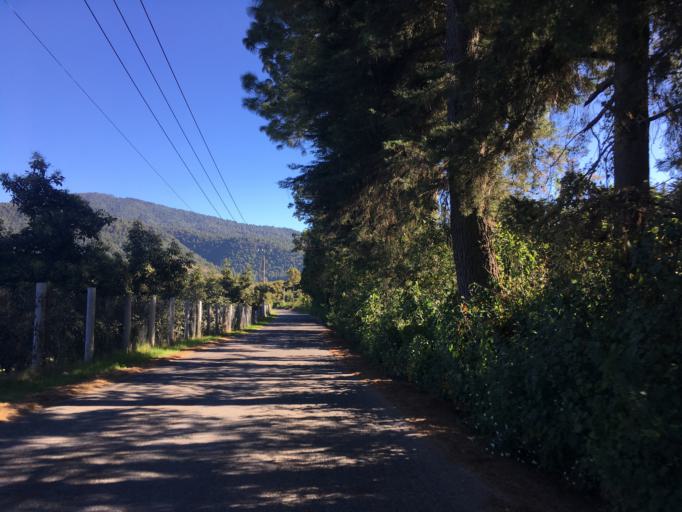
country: MX
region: Michoacan
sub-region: Zitacuaro
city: Macutzio
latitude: 19.4874
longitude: -100.3300
